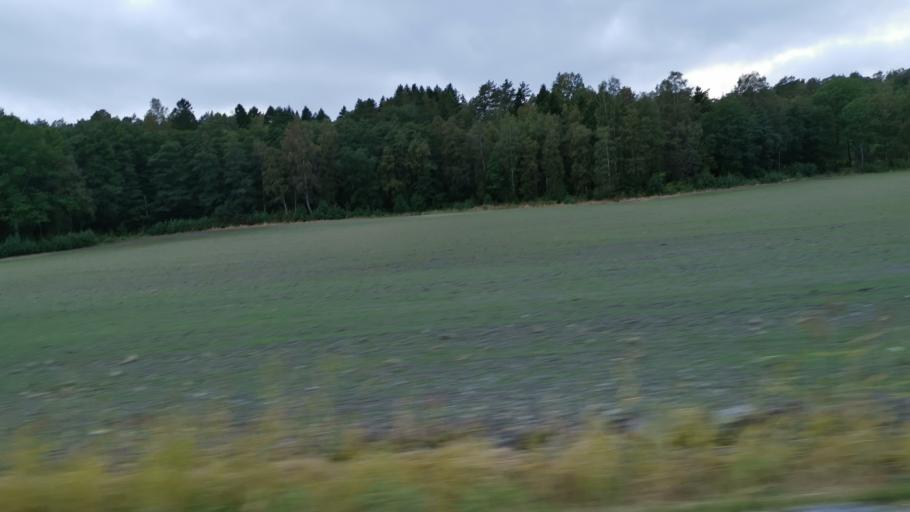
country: SE
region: Vaestra Goetaland
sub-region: Tanums Kommun
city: Tanumshede
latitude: 58.6261
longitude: 11.3514
